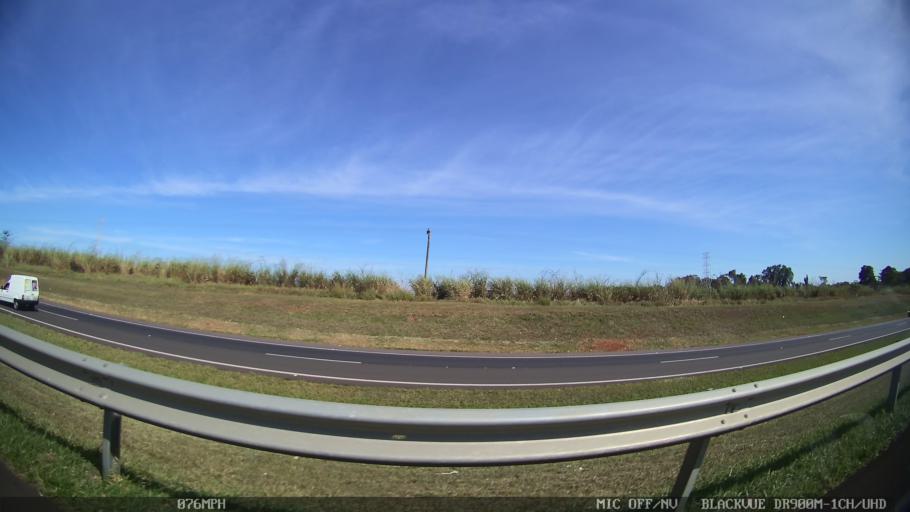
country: BR
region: Sao Paulo
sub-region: Pirassununga
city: Pirassununga
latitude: -21.9731
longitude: -47.4542
